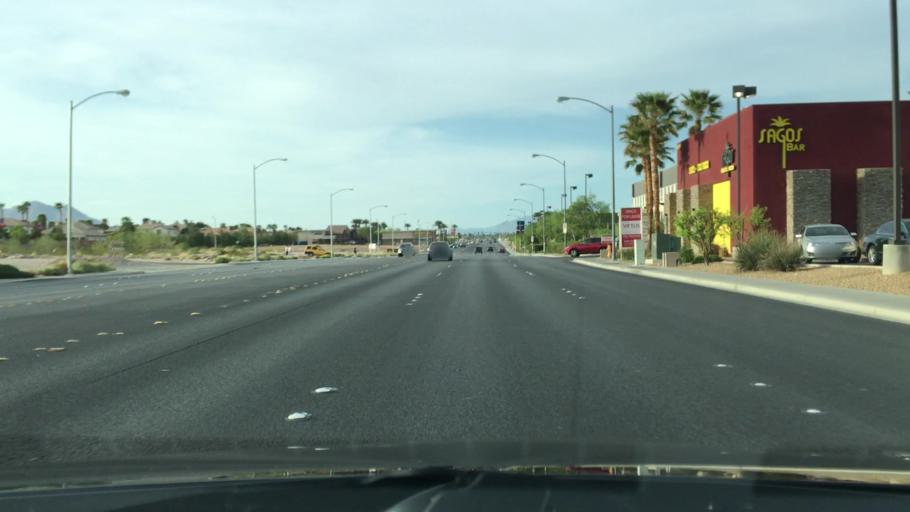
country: US
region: Nevada
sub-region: Clark County
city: Summerlin South
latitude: 36.1016
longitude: -115.2972
